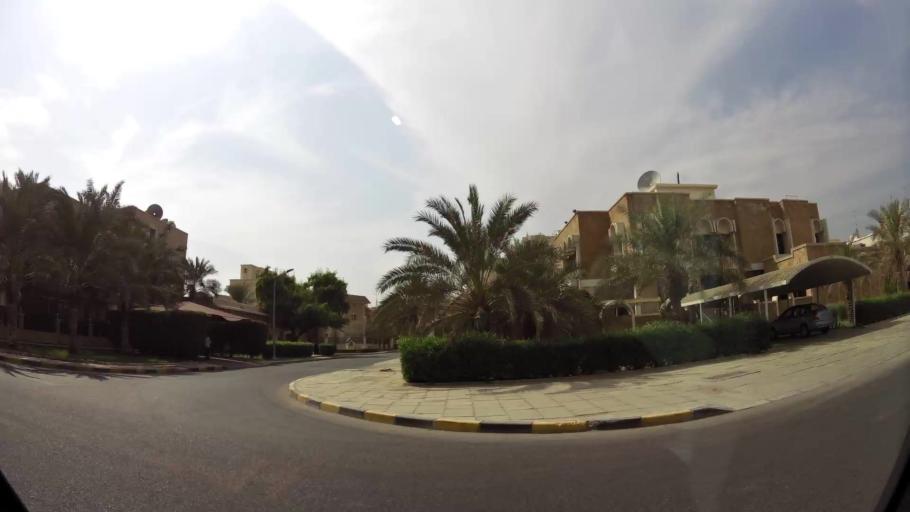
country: KW
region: Al Asimah
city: Kuwait City
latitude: 29.3567
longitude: 47.9873
